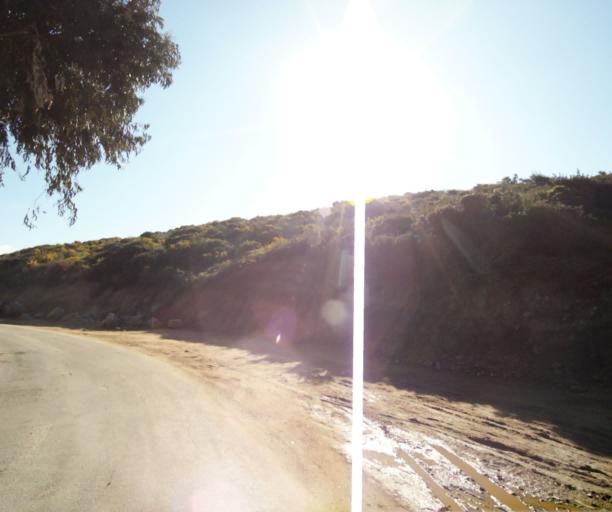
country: FR
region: Corsica
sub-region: Departement de la Corse-du-Sud
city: Propriano
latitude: 41.6713
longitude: 8.8912
